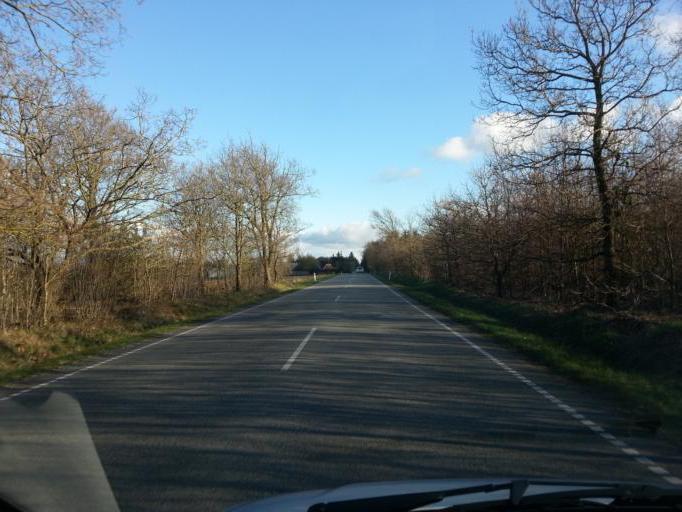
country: DK
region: Central Jutland
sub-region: Ringkobing-Skjern Kommune
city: Tarm
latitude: 55.8443
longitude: 8.5584
